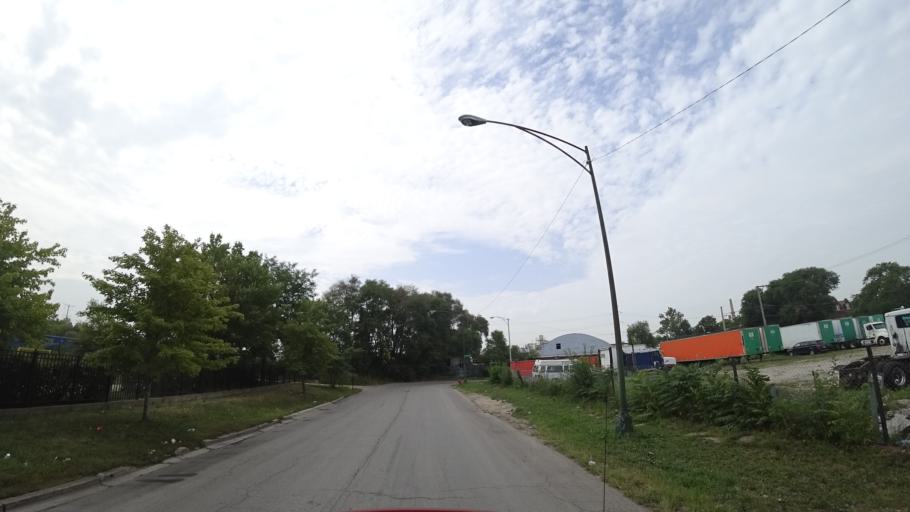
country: US
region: Illinois
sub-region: Cook County
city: Cicero
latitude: 41.8358
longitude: -87.7146
